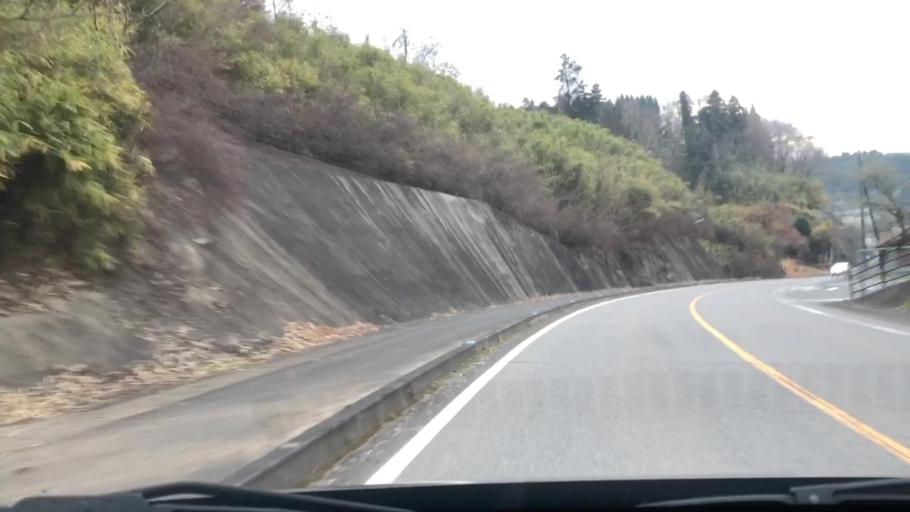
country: JP
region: Oita
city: Usuki
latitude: 33.0084
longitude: 131.6458
